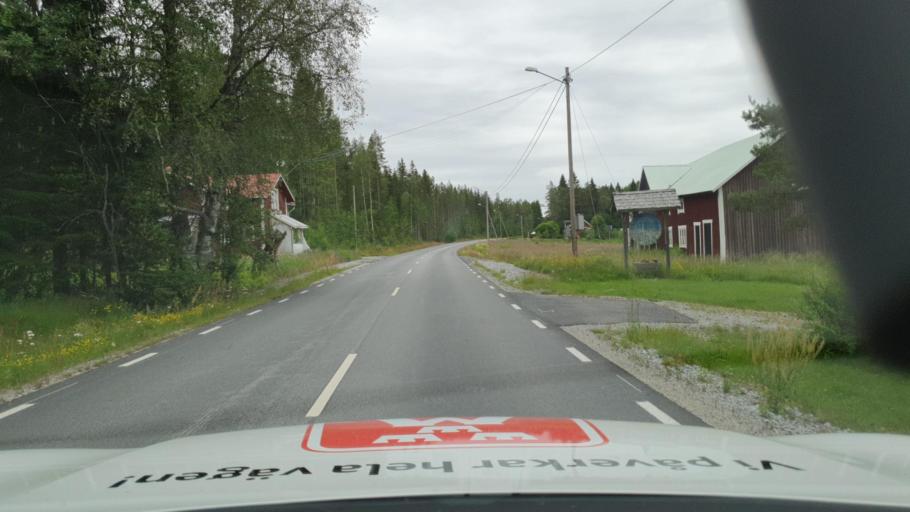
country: SE
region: Vaesterbotten
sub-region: Nordmalings Kommun
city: Nordmaling
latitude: 63.5236
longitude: 19.3606
